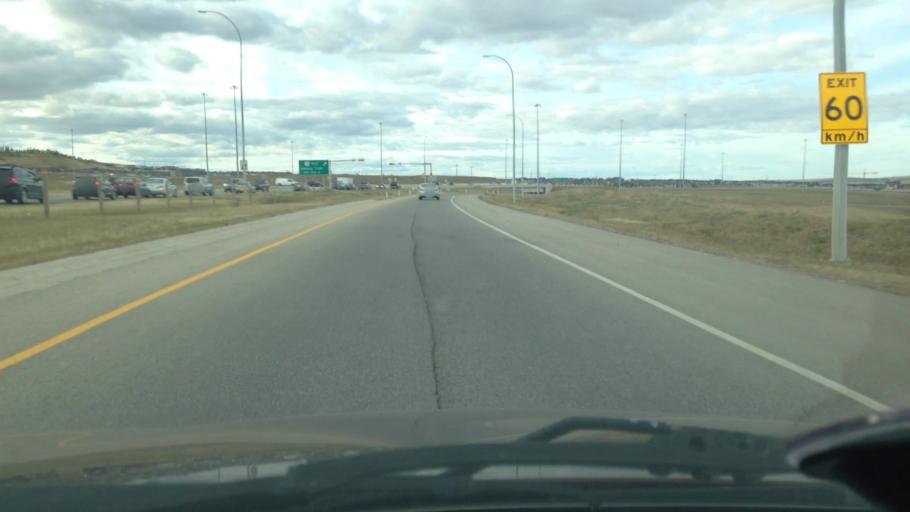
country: CA
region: Alberta
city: Calgary
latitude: 51.1489
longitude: -114.1374
